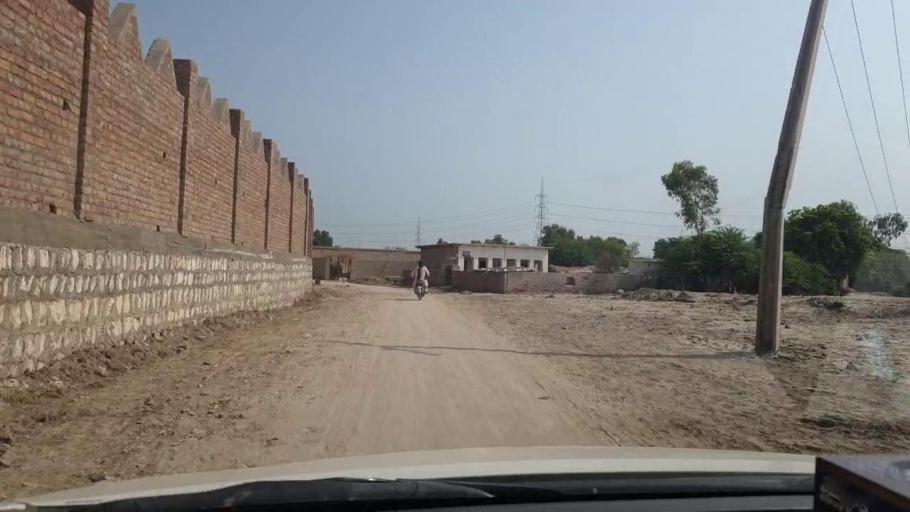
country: PK
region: Sindh
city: Shikarpur
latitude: 27.9676
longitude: 68.6660
